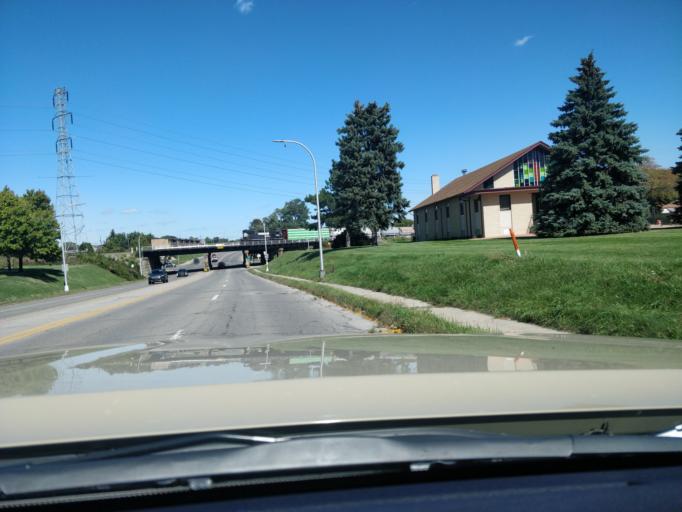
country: US
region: Michigan
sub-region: Wayne County
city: Allen Park
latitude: 42.2717
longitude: -83.1955
